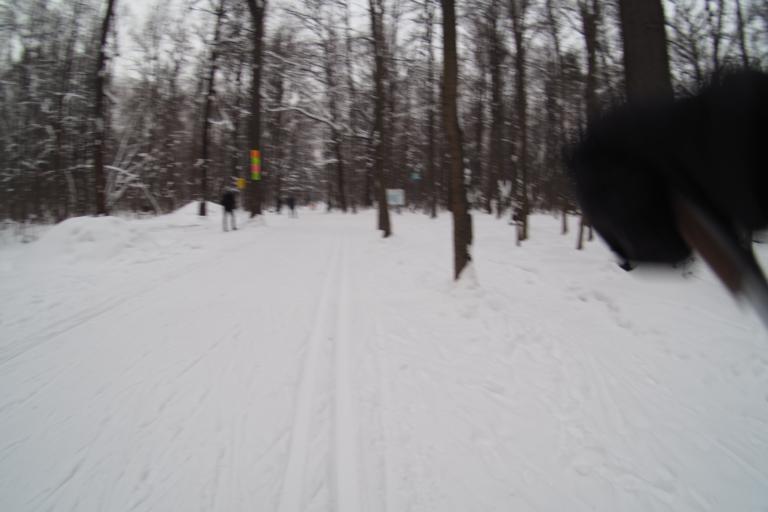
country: RU
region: Moscow
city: Ryazanskiy
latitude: 55.7658
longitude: 37.7715
